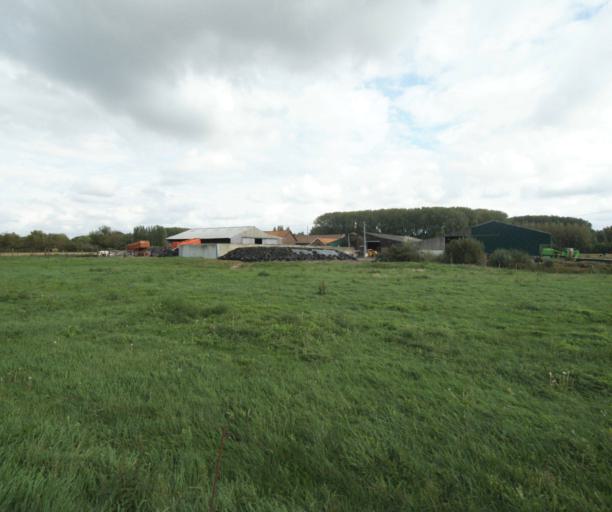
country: FR
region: Nord-Pas-de-Calais
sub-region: Departement du Nord
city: Ennetieres-en-Weppes
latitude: 50.6520
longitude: 2.9329
